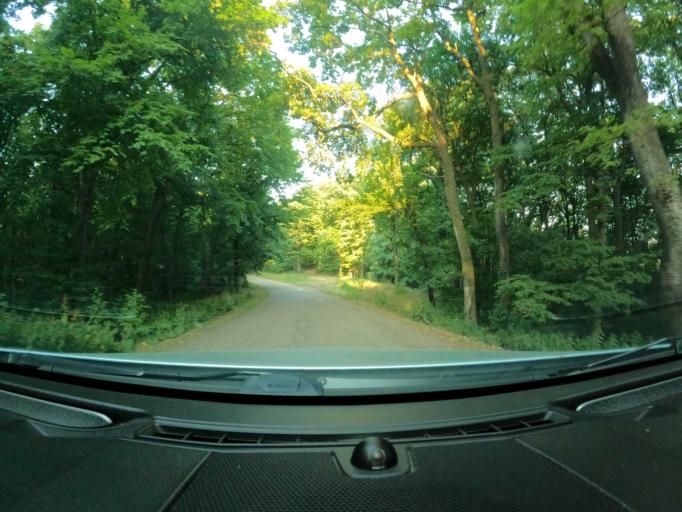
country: RS
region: Autonomna Pokrajina Vojvodina
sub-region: Juznobacki Okrug
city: Beocin
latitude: 45.1534
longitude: 19.7270
